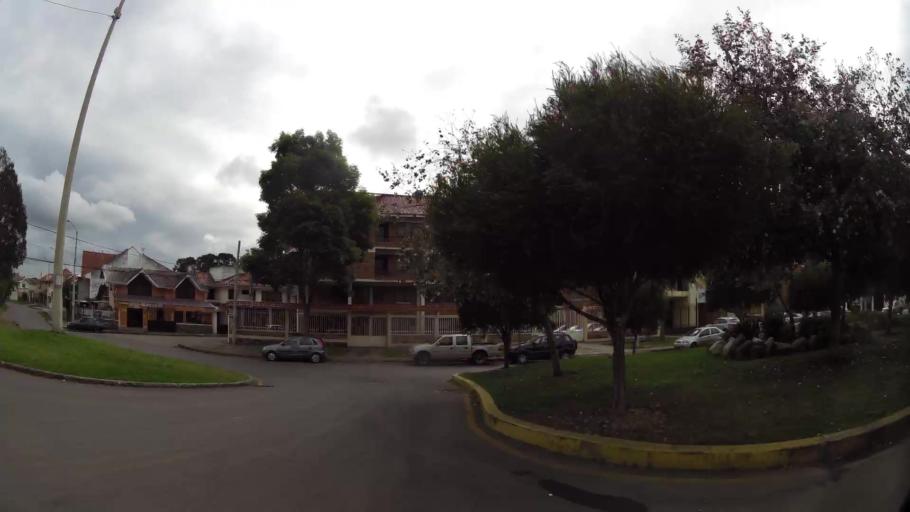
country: EC
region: Azuay
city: Cuenca
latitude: -2.9042
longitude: -78.9827
